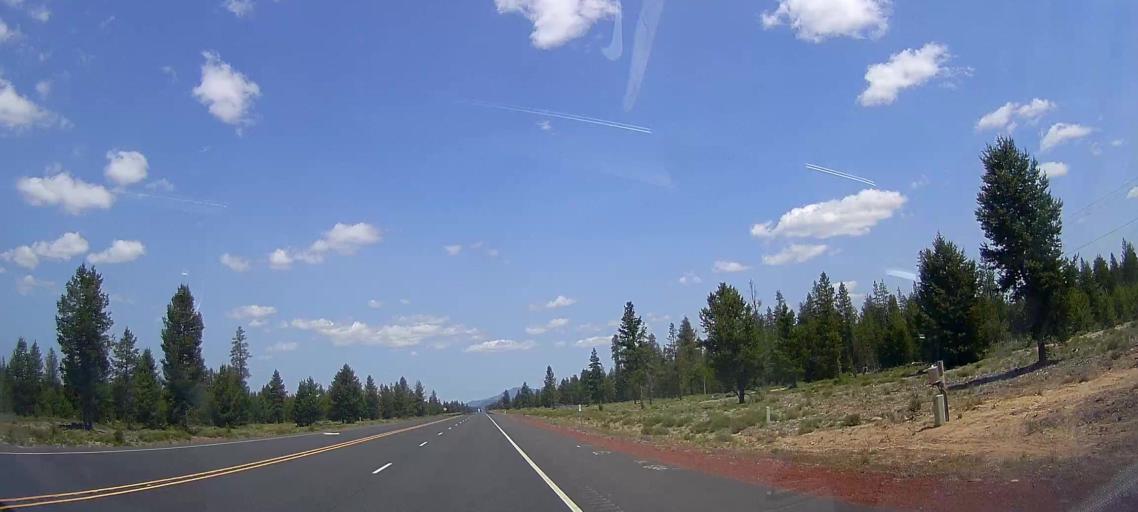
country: US
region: Oregon
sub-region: Deschutes County
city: La Pine
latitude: 43.1099
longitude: -121.8130
